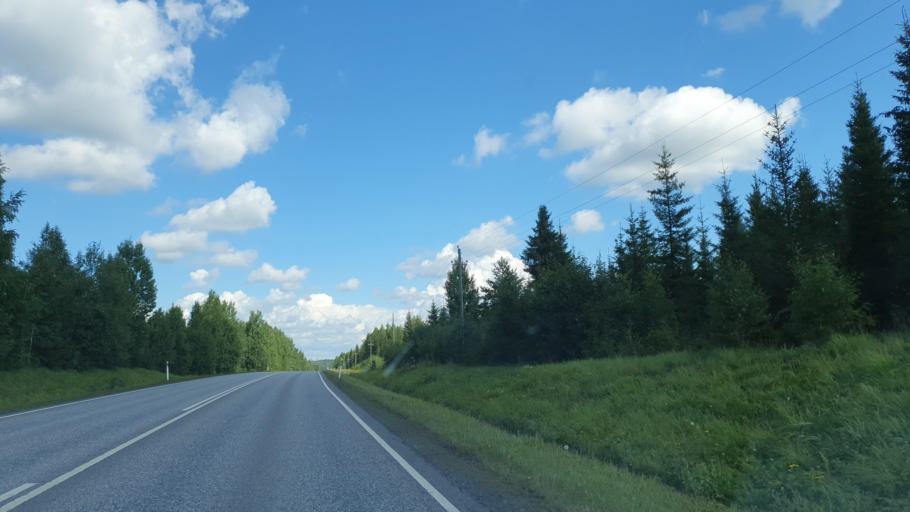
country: FI
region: Northern Savo
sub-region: Ylae-Savo
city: Sonkajaervi
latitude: 63.7121
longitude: 27.3605
